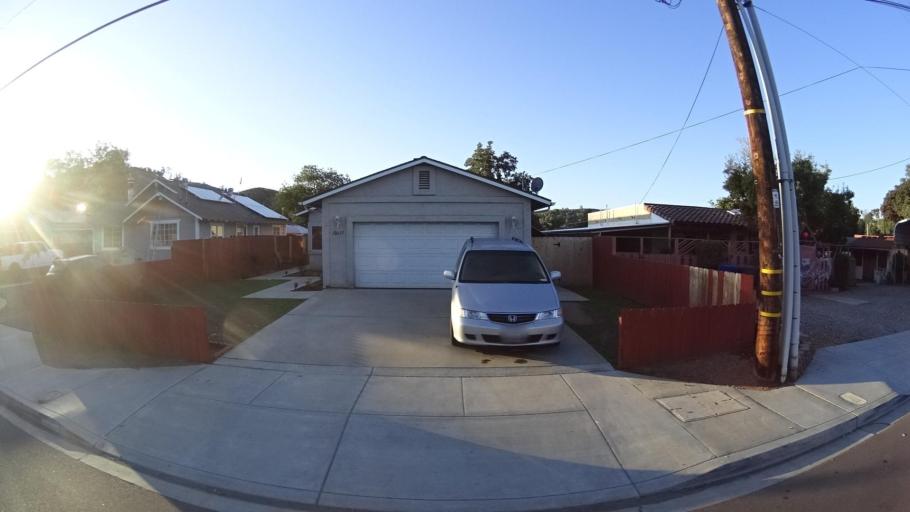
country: US
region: California
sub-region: San Diego County
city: Lakeside
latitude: 32.8554
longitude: -116.9189
